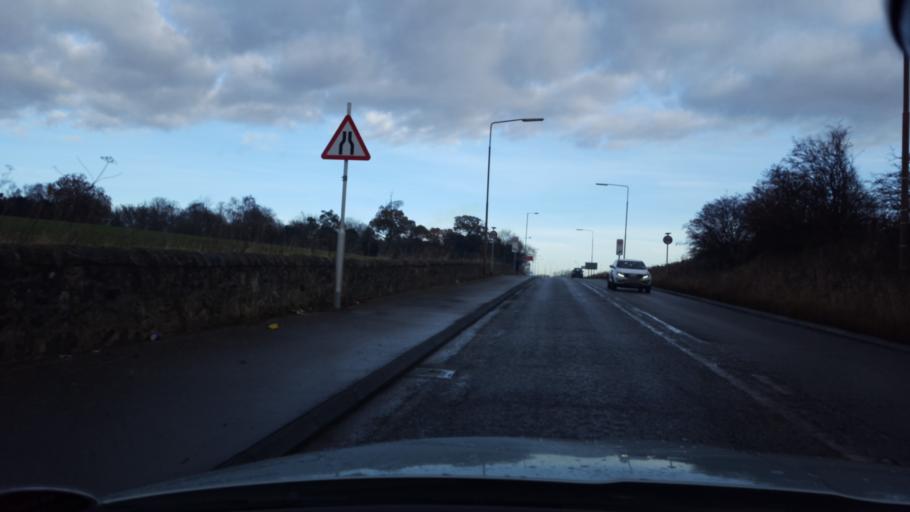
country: GB
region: Scotland
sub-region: Edinburgh
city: Queensferry
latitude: 55.9753
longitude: -3.3984
